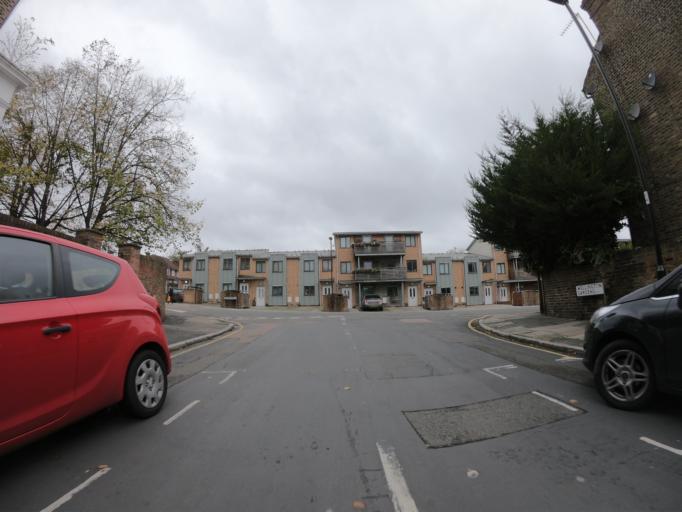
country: GB
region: England
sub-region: Greater London
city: Blackheath
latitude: 51.4831
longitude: 0.0297
